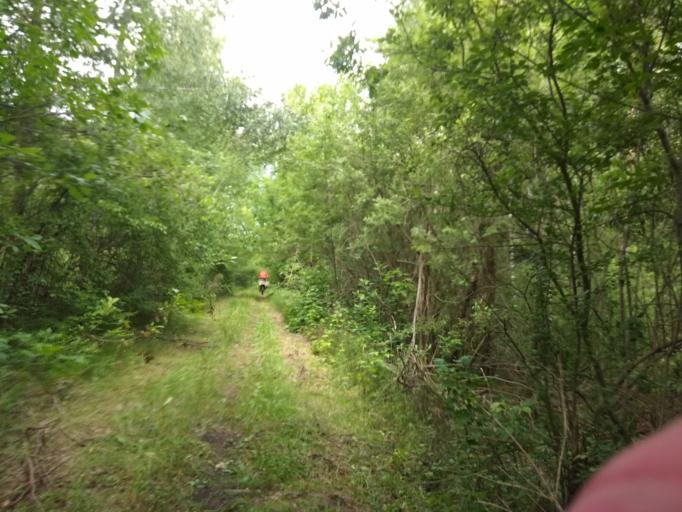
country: RU
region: Moskovskaya
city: Misheronskiy
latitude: 55.7015
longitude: 39.7200
